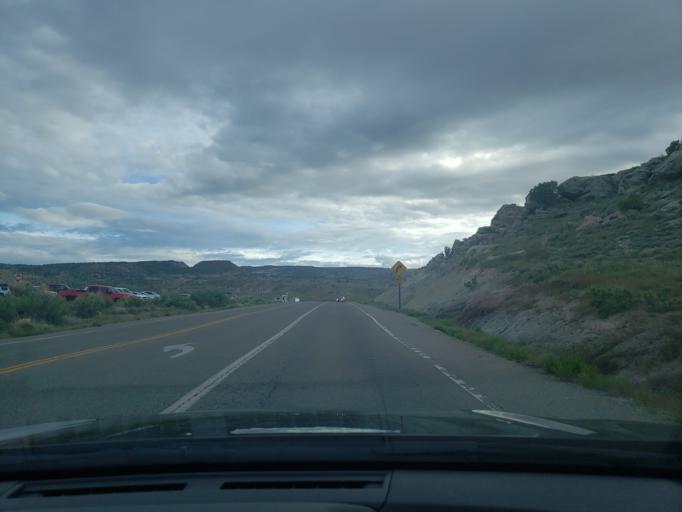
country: US
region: Colorado
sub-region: Mesa County
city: Redlands
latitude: 39.0510
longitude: -108.6051
